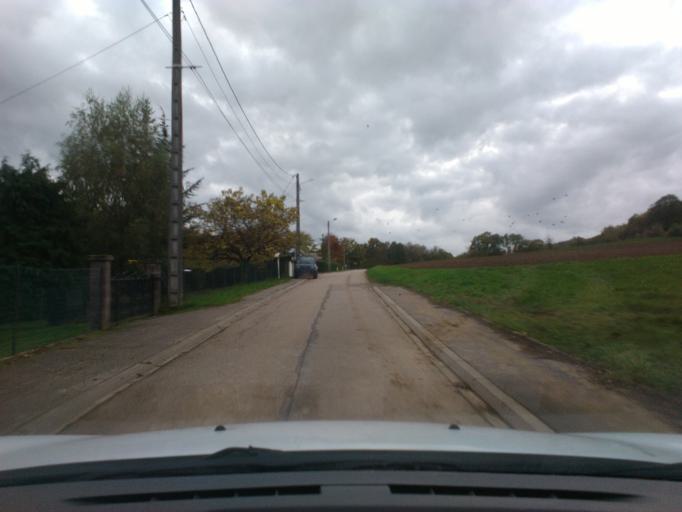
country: FR
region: Lorraine
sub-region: Departement des Vosges
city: Mirecourt
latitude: 48.3421
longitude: 6.1366
